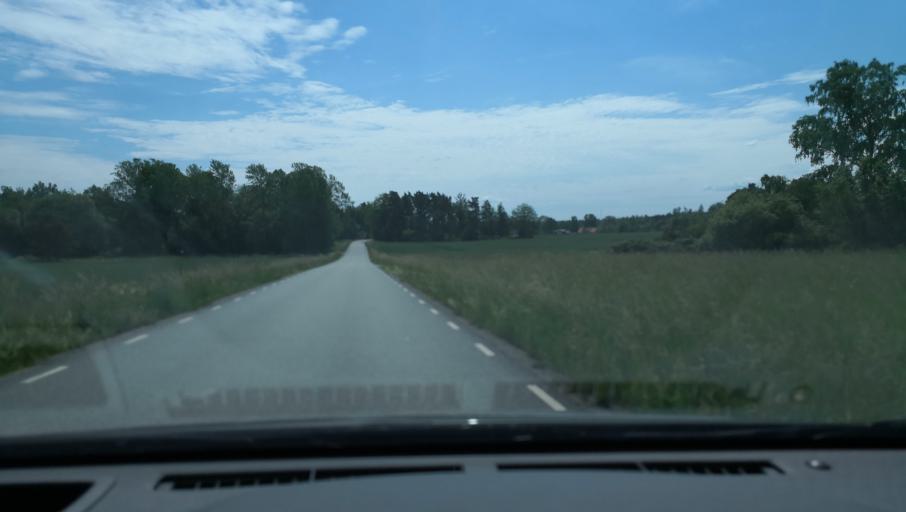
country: SE
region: Uppsala
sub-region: Habo Kommun
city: Balsta
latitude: 59.6797
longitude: 17.4668
